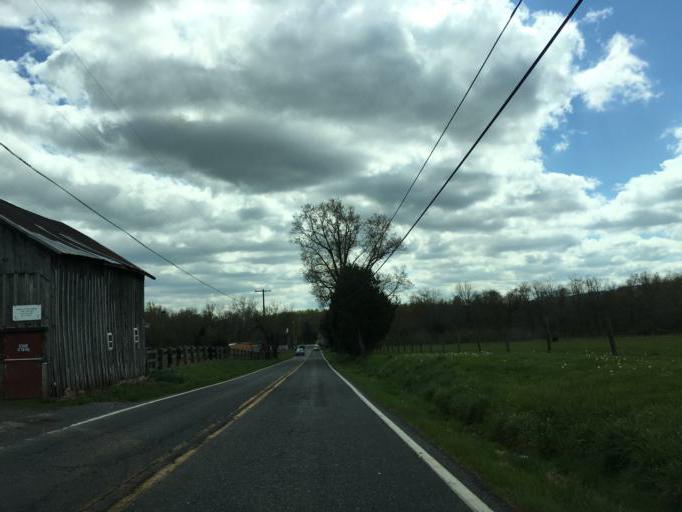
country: US
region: Maryland
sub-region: Frederick County
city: Thurmont
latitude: 39.5965
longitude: -77.3951
